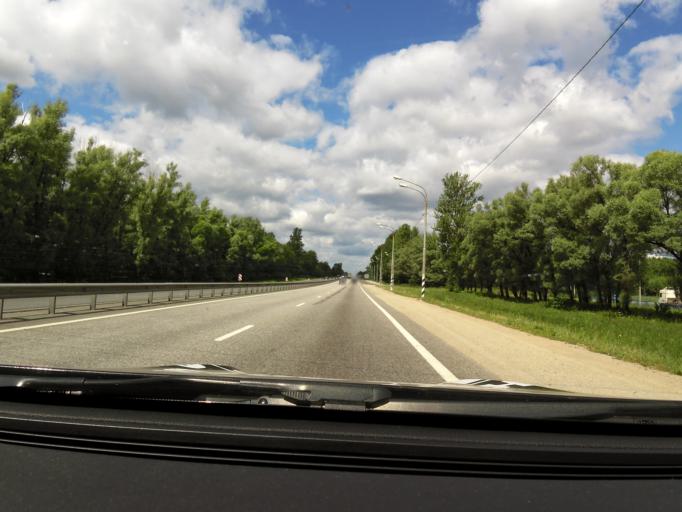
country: RU
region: Tverskaya
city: Likhoslavl'
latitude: 56.9847
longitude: 35.2316
